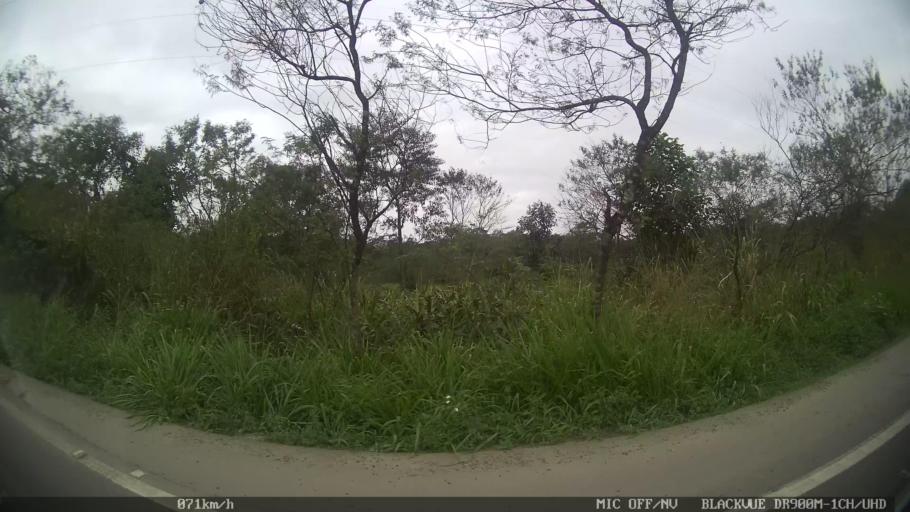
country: BR
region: Santa Catarina
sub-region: Joinville
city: Joinville
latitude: -26.2576
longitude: -48.9079
